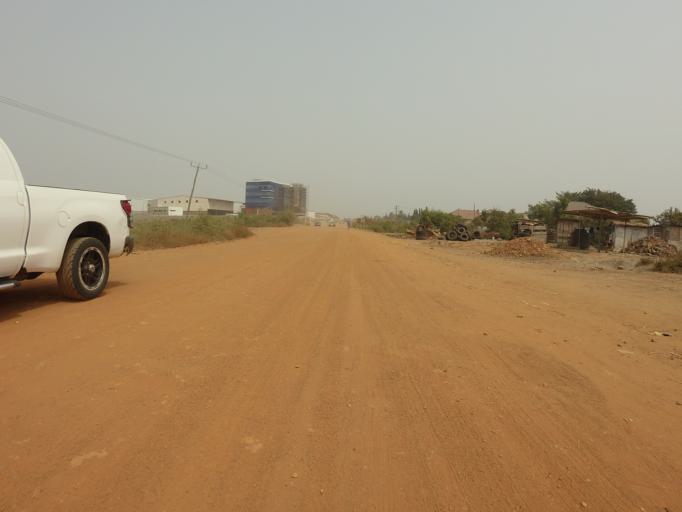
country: GH
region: Greater Accra
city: Nungua
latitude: 5.6462
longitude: -0.1018
